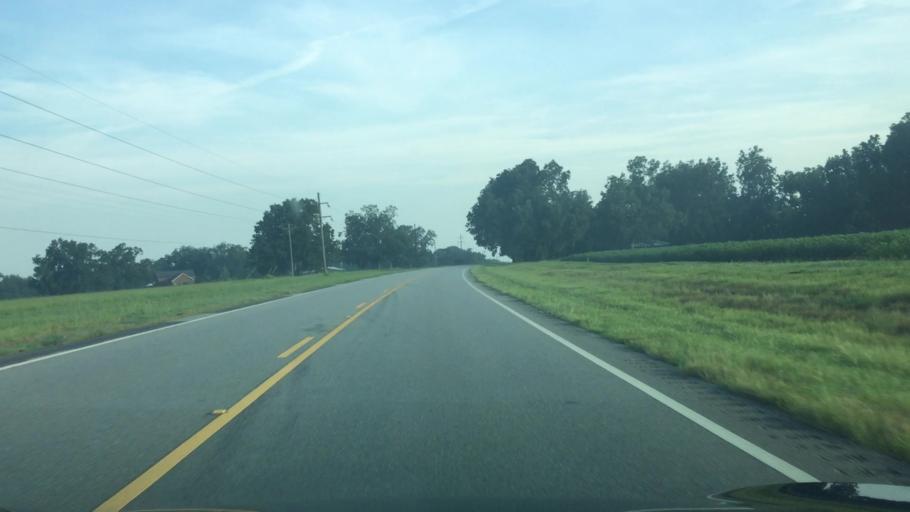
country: US
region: Alabama
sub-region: Covington County
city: Florala
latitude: 31.0474
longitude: -86.3858
